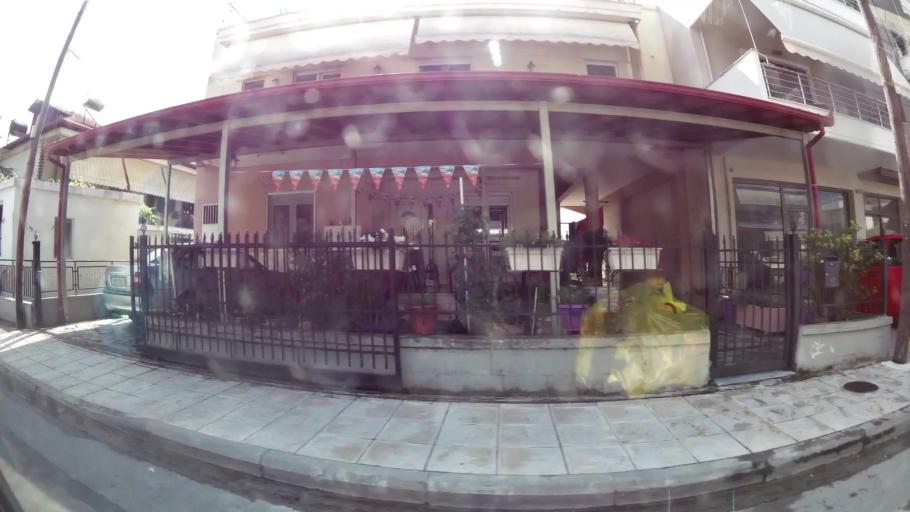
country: GR
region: Central Macedonia
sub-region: Nomos Pierias
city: Katerini
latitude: 40.2818
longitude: 22.5077
